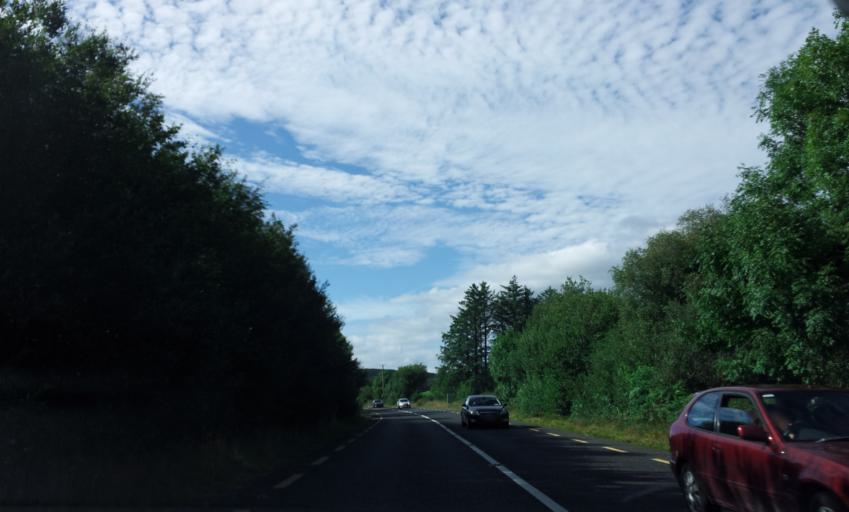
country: IE
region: Munster
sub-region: County Cork
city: Macroom
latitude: 51.9075
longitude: -9.0096
